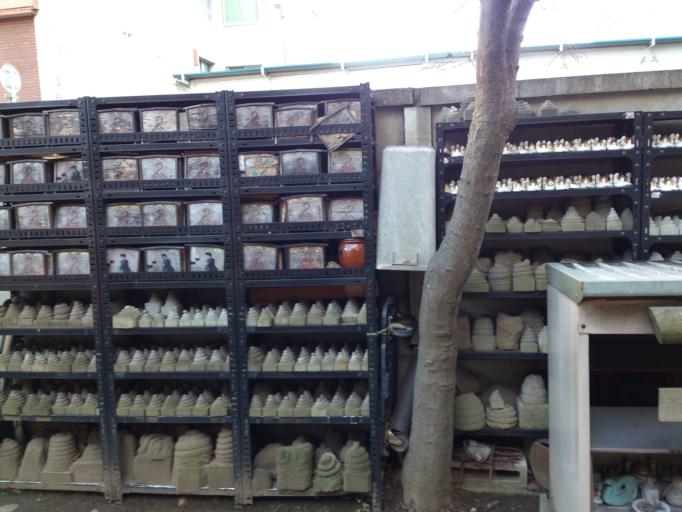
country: JP
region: Chiba
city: Matsudo
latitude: 35.7878
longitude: 139.9041
